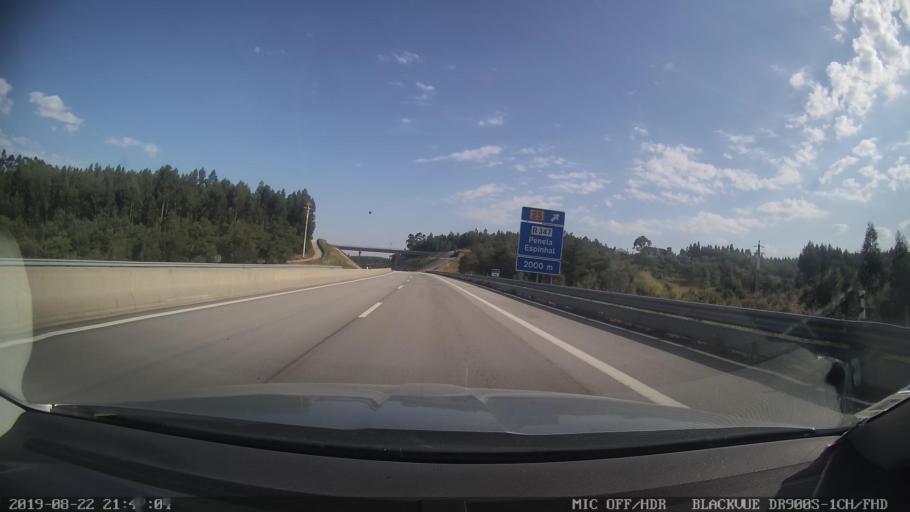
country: PT
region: Coimbra
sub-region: Penela
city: Penela
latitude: 39.9987
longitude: -8.3622
